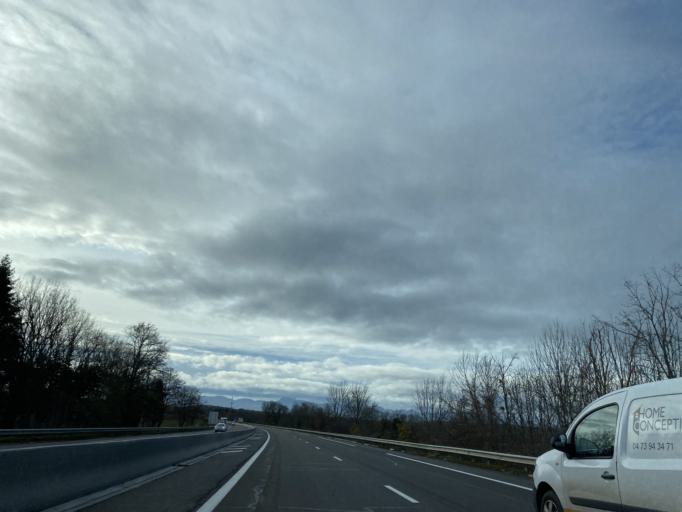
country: FR
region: Auvergne
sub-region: Departement du Puy-de-Dome
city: Culhat
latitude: 45.8398
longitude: 3.3114
